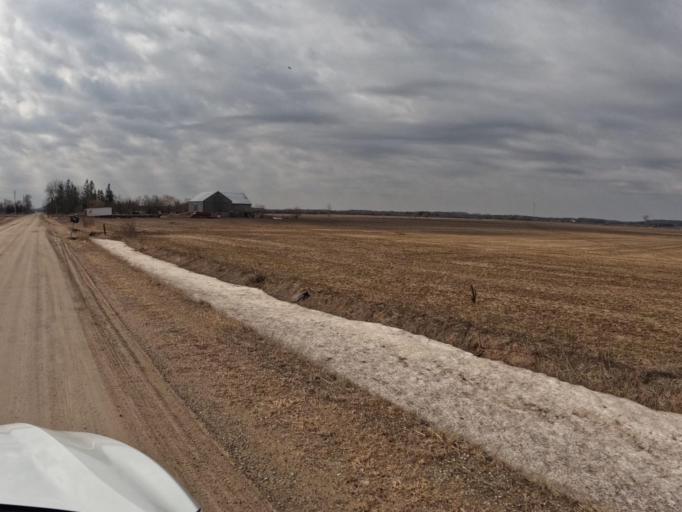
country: CA
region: Ontario
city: Orangeville
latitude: 43.9145
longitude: -80.2165
